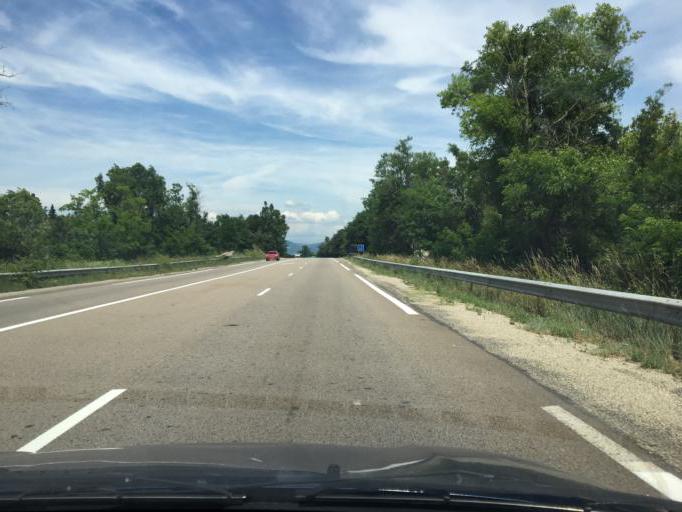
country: FR
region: Rhone-Alpes
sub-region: Departement de la Drome
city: Malataverne
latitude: 44.4872
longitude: 4.7539
